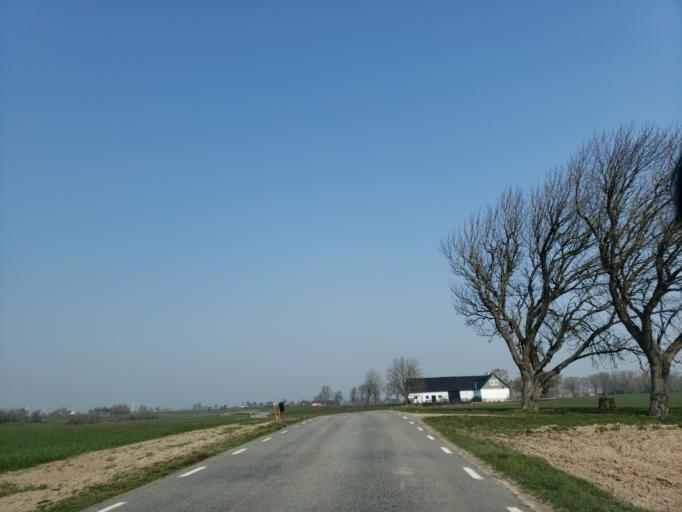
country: SE
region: Skane
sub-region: Simrishamns Kommun
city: Simrishamn
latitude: 55.4951
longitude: 14.2240
